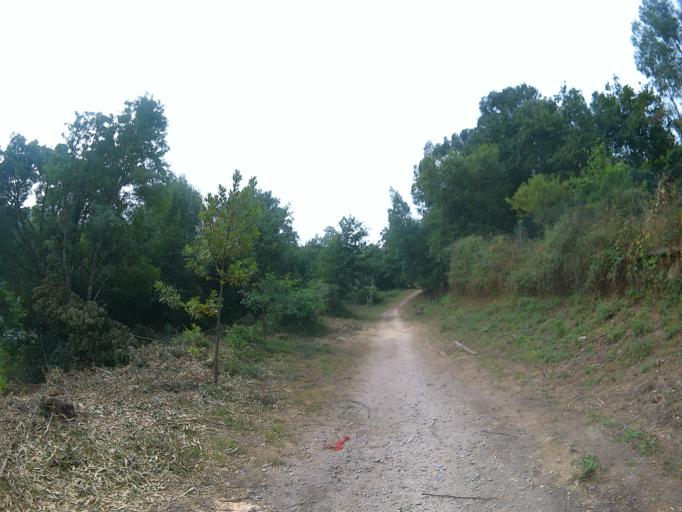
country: PT
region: Viana do Castelo
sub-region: Ponte de Lima
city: Ponte de Lima
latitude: 41.7772
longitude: -8.5557
